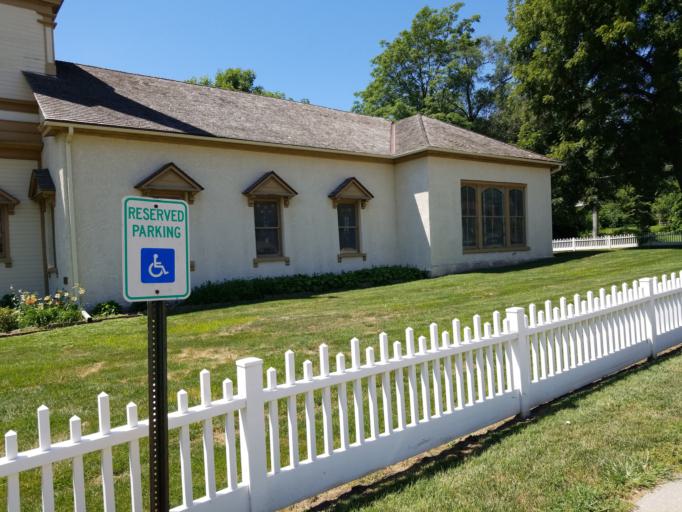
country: US
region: Nebraska
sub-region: Sarpy County
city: Bellevue
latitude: 41.1395
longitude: -95.8939
